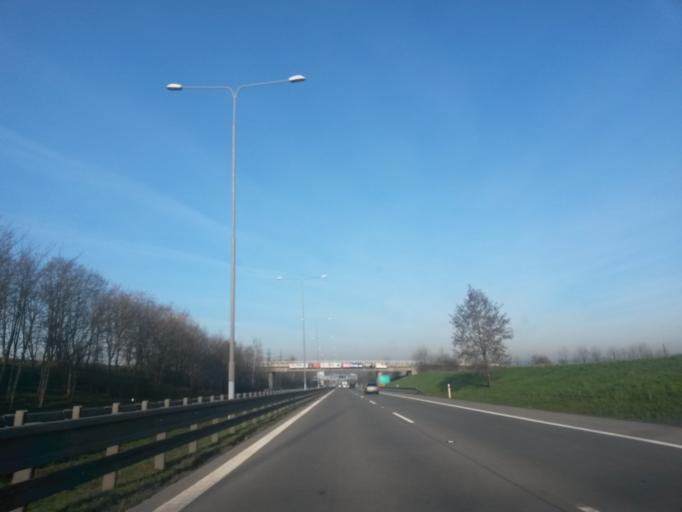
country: CZ
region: Central Bohemia
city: Trebotov
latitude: 50.0239
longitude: 14.3188
